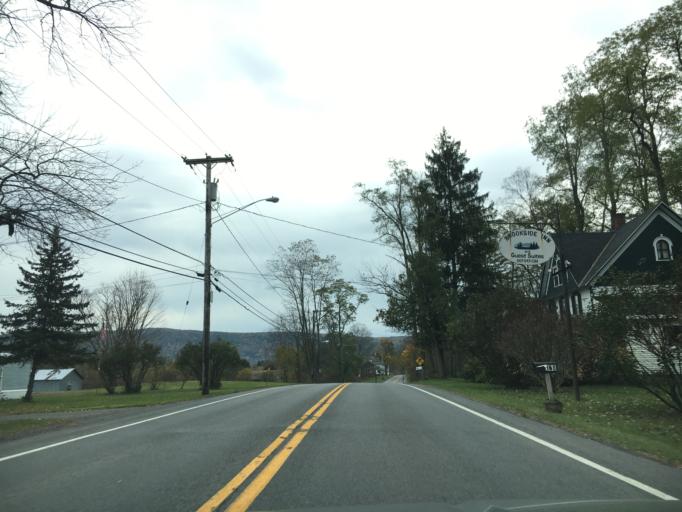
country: US
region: New York
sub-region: Otsego County
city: Cooperstown
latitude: 42.5960
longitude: -74.9466
